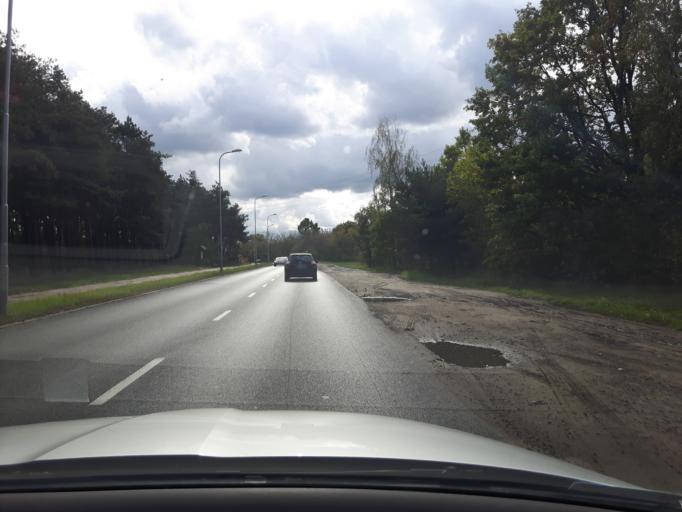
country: PL
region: Masovian Voivodeship
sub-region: Warszawa
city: Rembertow
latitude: 52.2317
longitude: 21.1437
